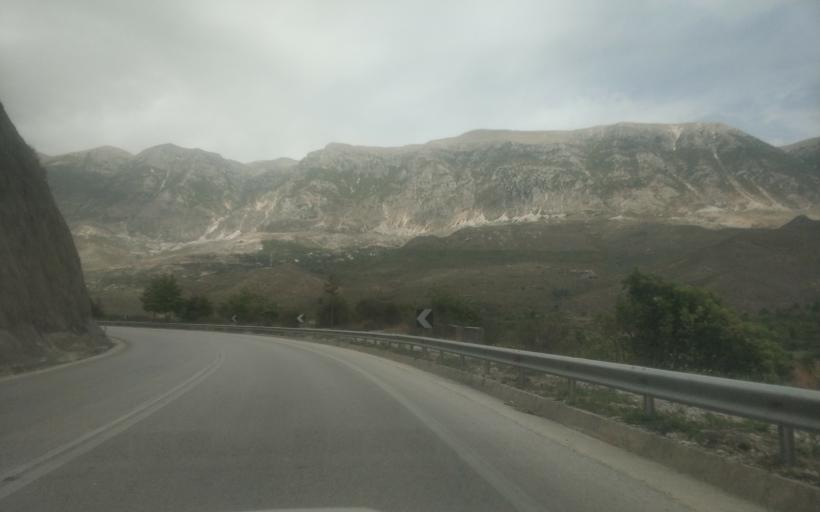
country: AL
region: Gjirokaster
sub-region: Rrethi i Gjirokastres
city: Picar
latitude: 40.2206
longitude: 20.0867
